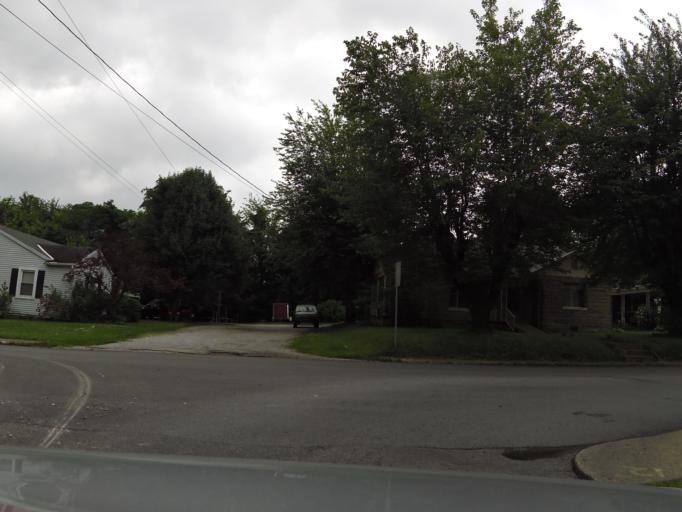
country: US
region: Kentucky
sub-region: Hopkins County
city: Madisonville
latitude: 37.3178
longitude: -87.4971
